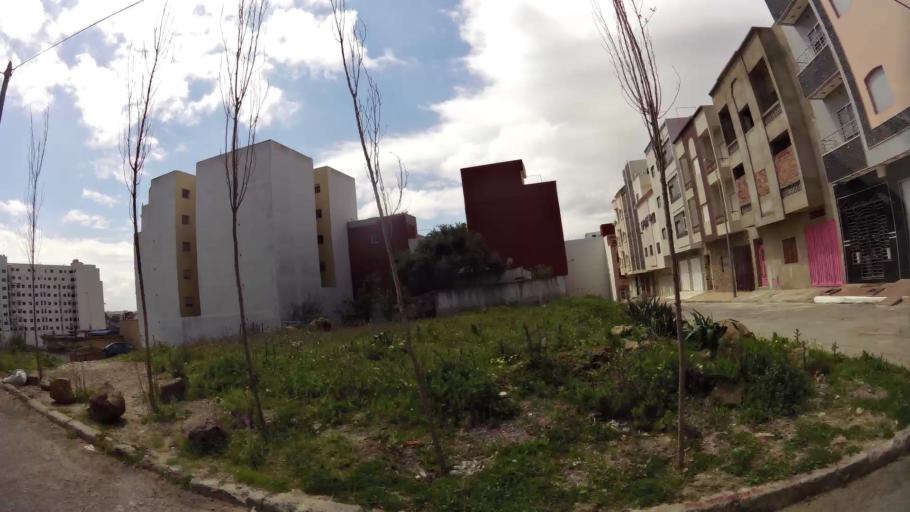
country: MA
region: Tanger-Tetouan
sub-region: Tanger-Assilah
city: Tangier
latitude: 35.7686
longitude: -5.8455
